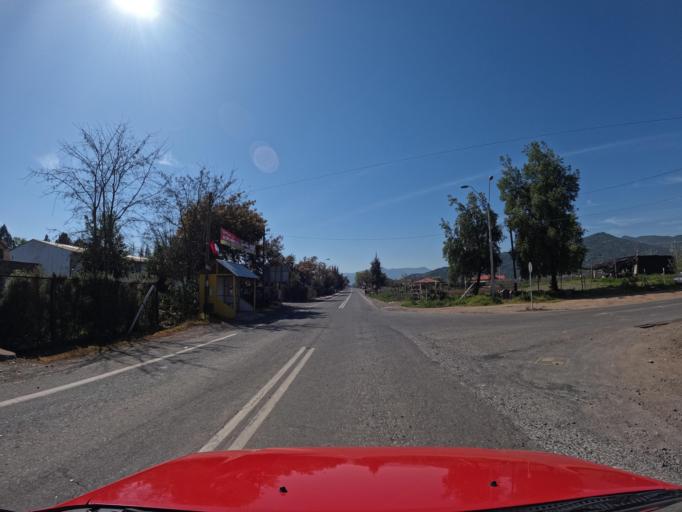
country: CL
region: Maule
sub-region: Provincia de Curico
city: Rauco
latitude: -35.0520
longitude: -71.4768
